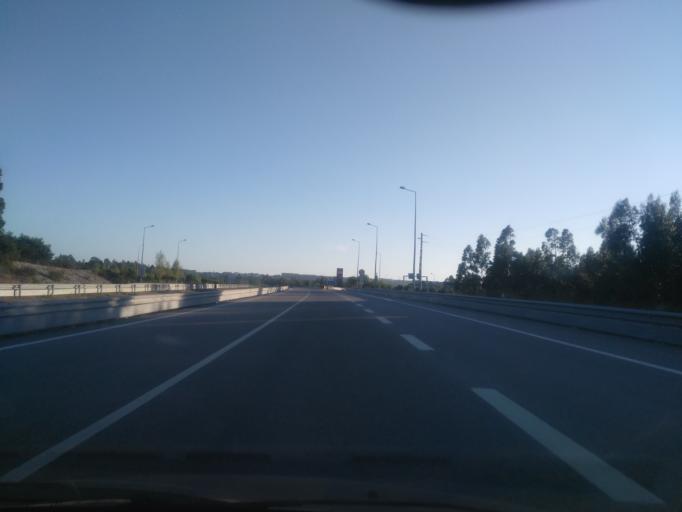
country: PT
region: Coimbra
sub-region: Figueira da Foz
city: Alhadas
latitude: 40.2148
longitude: -8.8089
